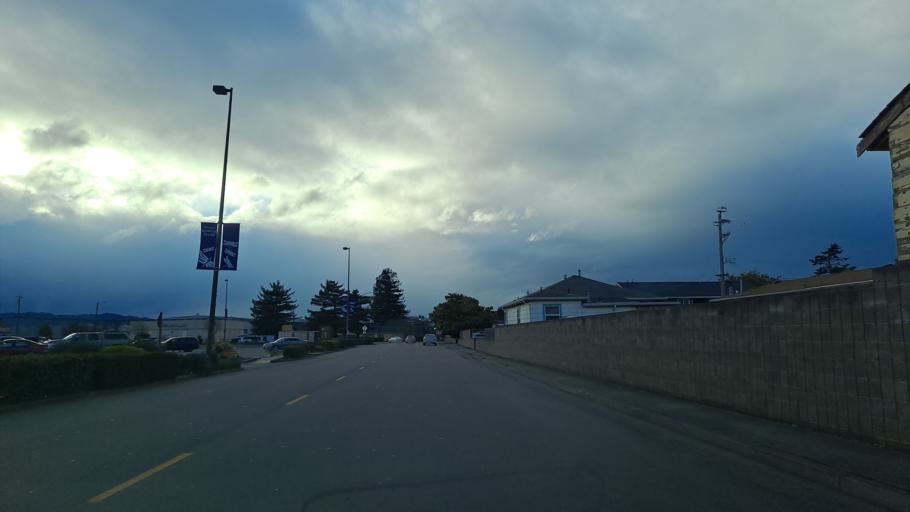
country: US
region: California
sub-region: Humboldt County
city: Fortuna
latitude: 40.5848
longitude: -124.1450
